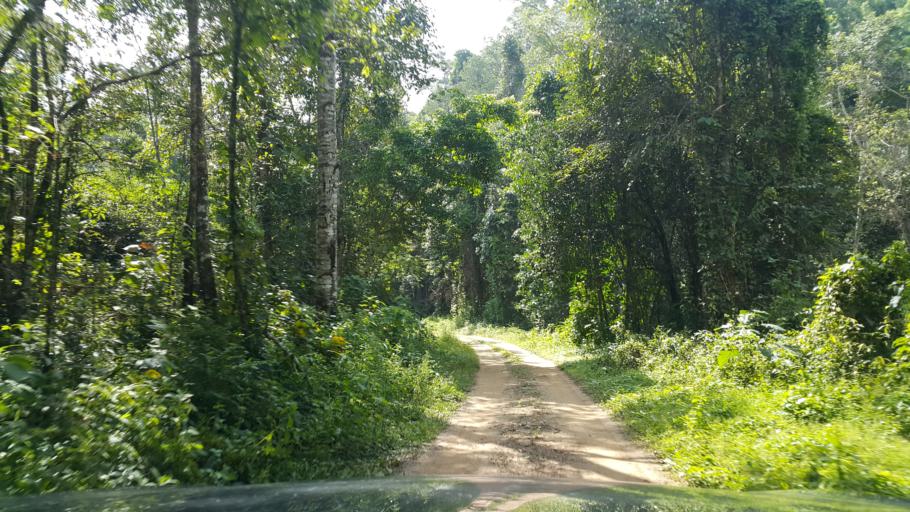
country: TH
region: Chiang Mai
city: Phrao
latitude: 19.0917
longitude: 99.2592
